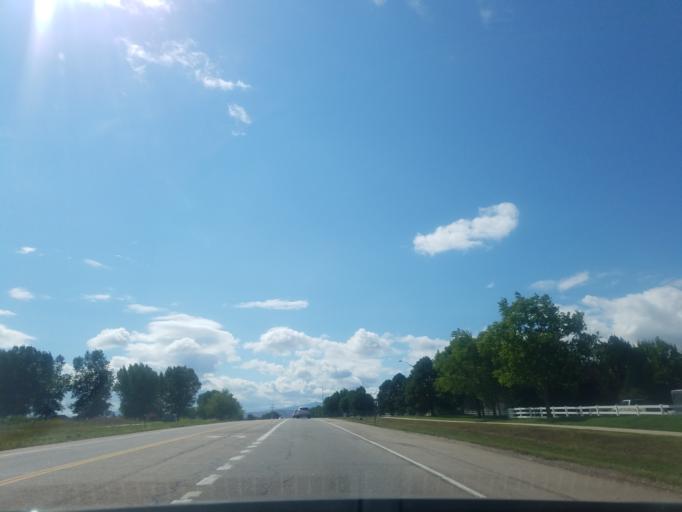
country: US
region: Colorado
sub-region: Larimer County
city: Loveland
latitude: 40.4801
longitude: -105.0436
